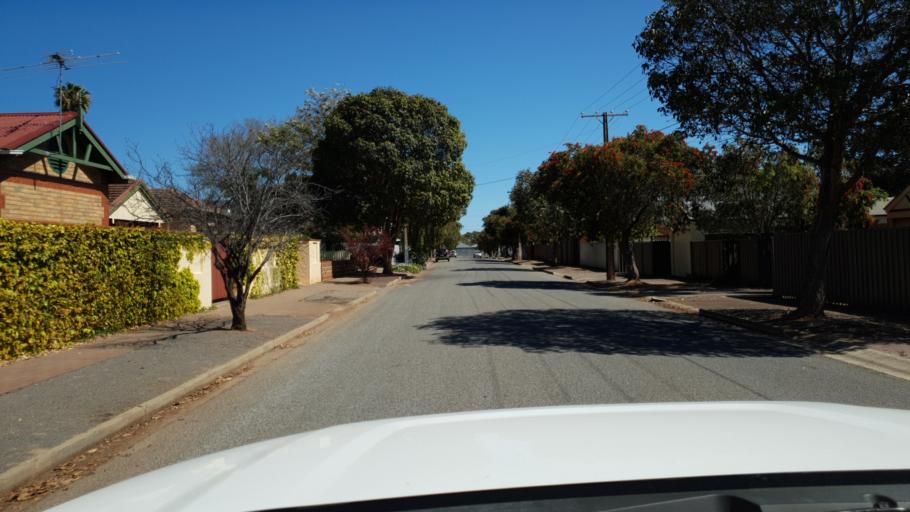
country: AU
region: South Australia
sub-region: Holdfast Bay
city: Seacliff Park
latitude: -35.0265
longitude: 138.5264
